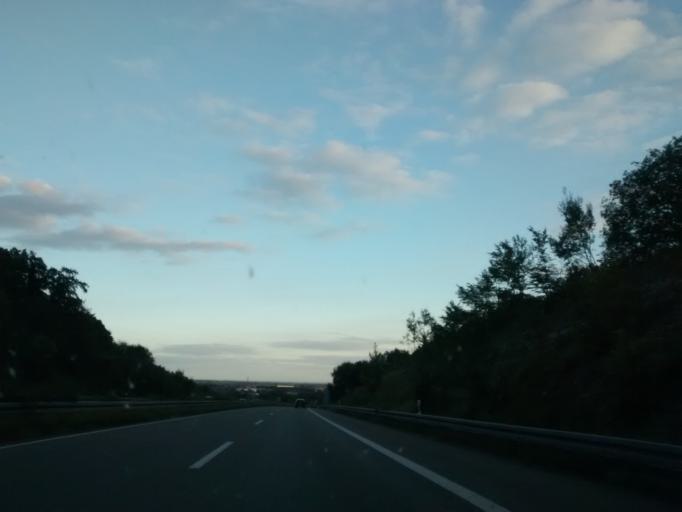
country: DE
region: Lower Saxony
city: Bad Rothenfelde
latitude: 52.1331
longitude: 8.1704
